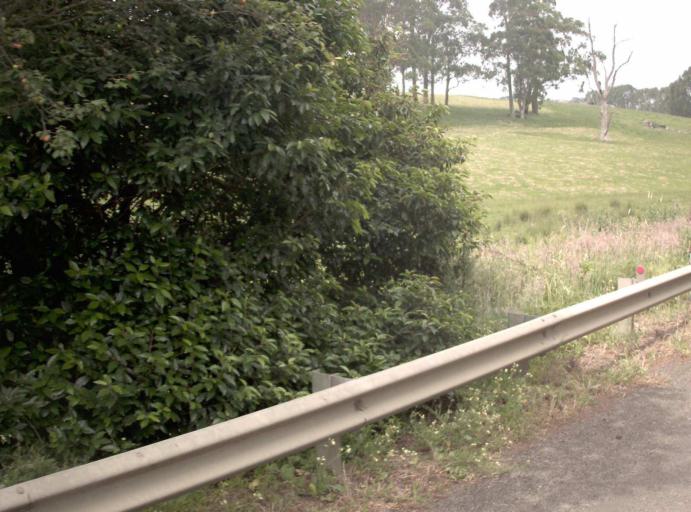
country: AU
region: Victoria
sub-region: Latrobe
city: Moe
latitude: -38.4007
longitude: 146.0983
